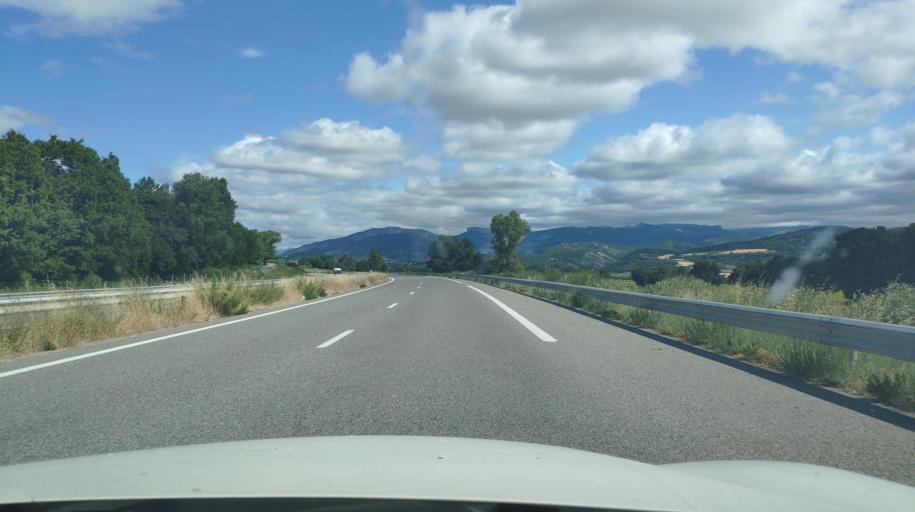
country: FR
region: Provence-Alpes-Cote d'Azur
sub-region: Departement des Alpes-de-Haute-Provence
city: Volonne
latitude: 44.1026
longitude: 5.9947
